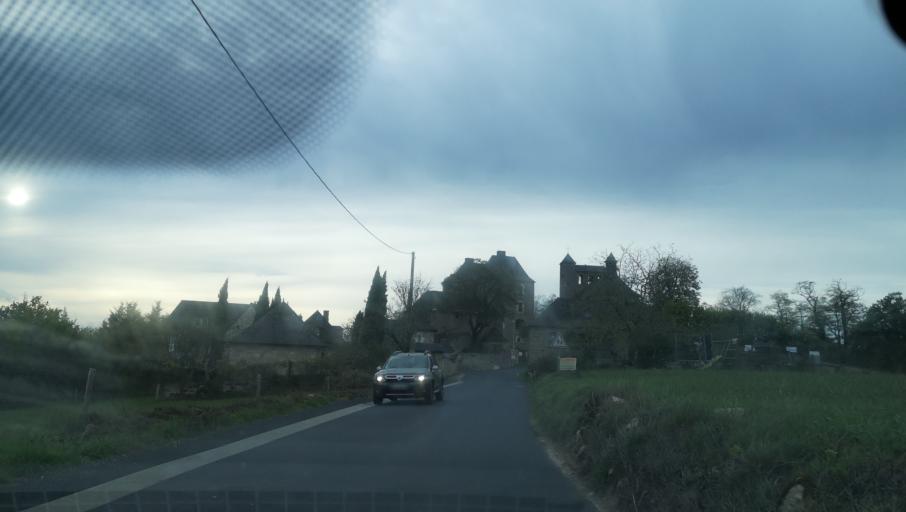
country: FR
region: Limousin
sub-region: Departement de la Correze
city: Brive-la-Gaillarde
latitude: 45.1035
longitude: 1.5279
